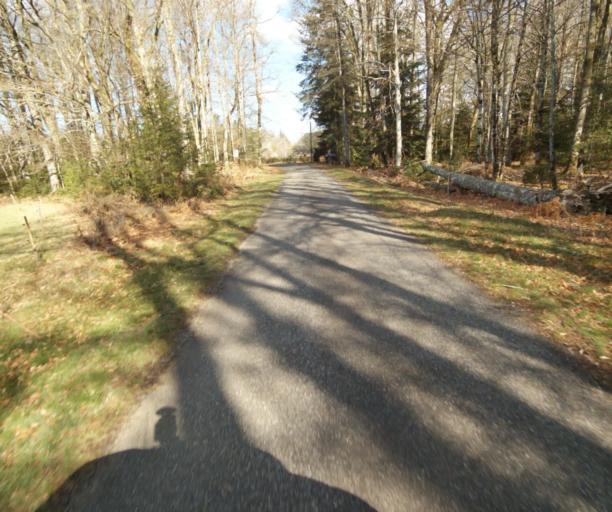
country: FR
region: Limousin
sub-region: Departement de la Correze
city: Laguenne
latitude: 45.2454
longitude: 1.9121
